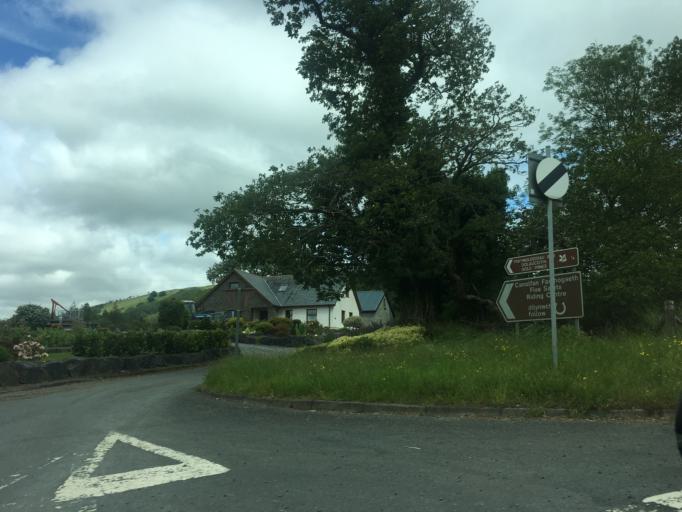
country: GB
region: Wales
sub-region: Carmarthenshire
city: Llansawel
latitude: 52.0453
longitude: -3.9569
